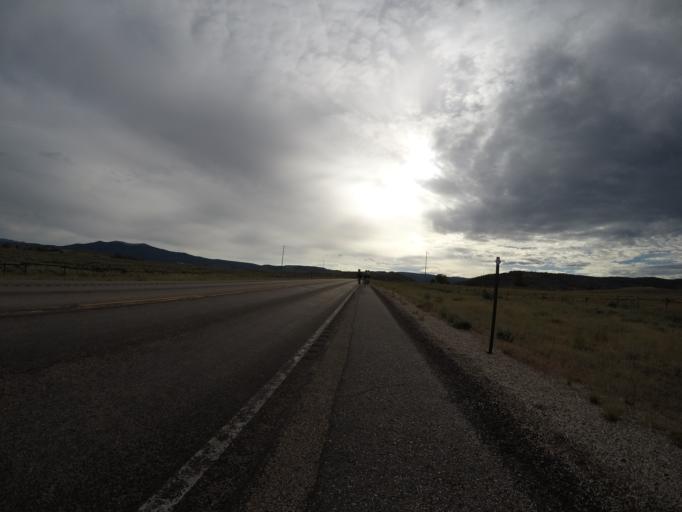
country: US
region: Wyoming
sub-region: Carbon County
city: Saratoga
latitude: 41.3581
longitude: -106.5926
